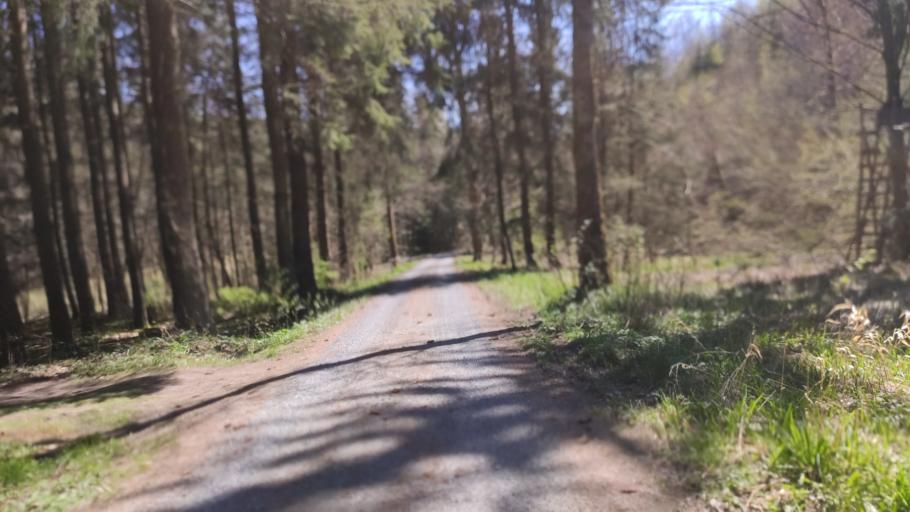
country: DE
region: Bavaria
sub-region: Upper Franconia
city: Nordhalben
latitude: 50.3619
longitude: 11.4816
